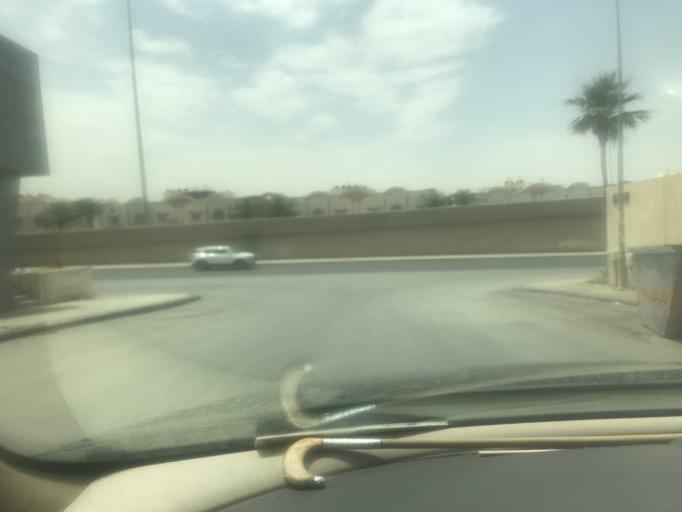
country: SA
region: Ar Riyad
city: Riyadh
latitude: 24.7883
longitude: 46.7035
